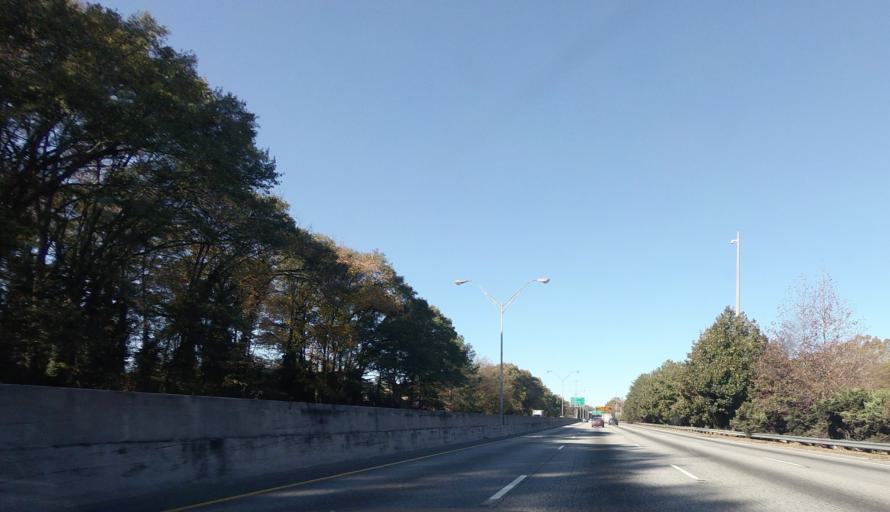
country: US
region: Georgia
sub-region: Fulton County
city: Atlanta
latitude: 33.7515
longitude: -84.4572
